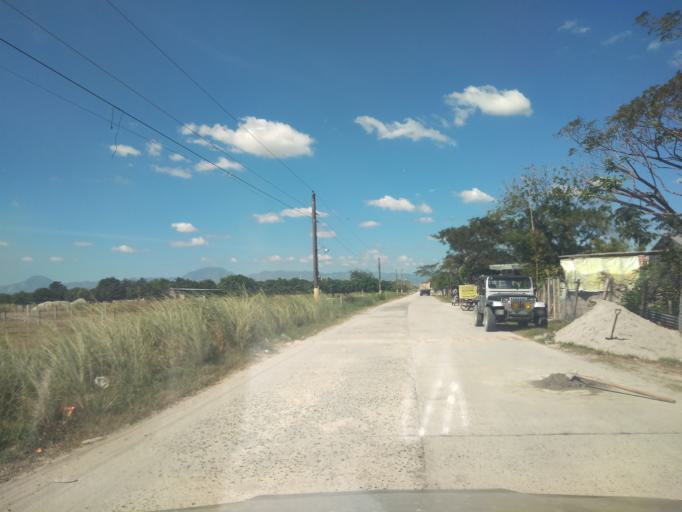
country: PH
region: Central Luzon
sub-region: Province of Pampanga
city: Balas
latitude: 15.0547
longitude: 120.6039
